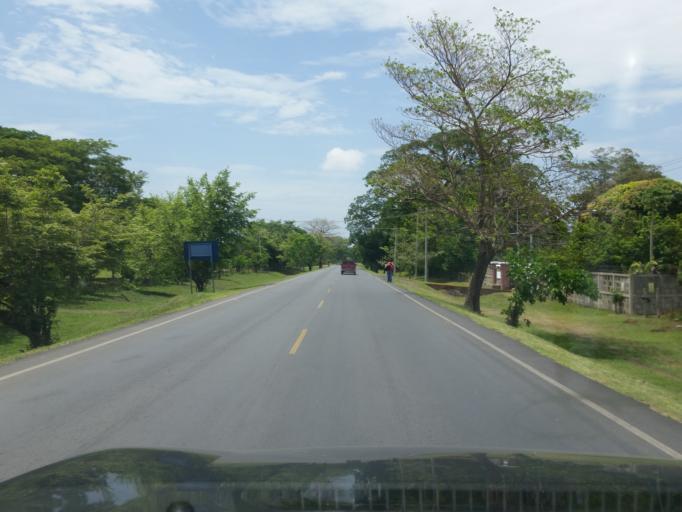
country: NI
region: Granada
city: Nandaime
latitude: 11.7497
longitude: -86.0329
